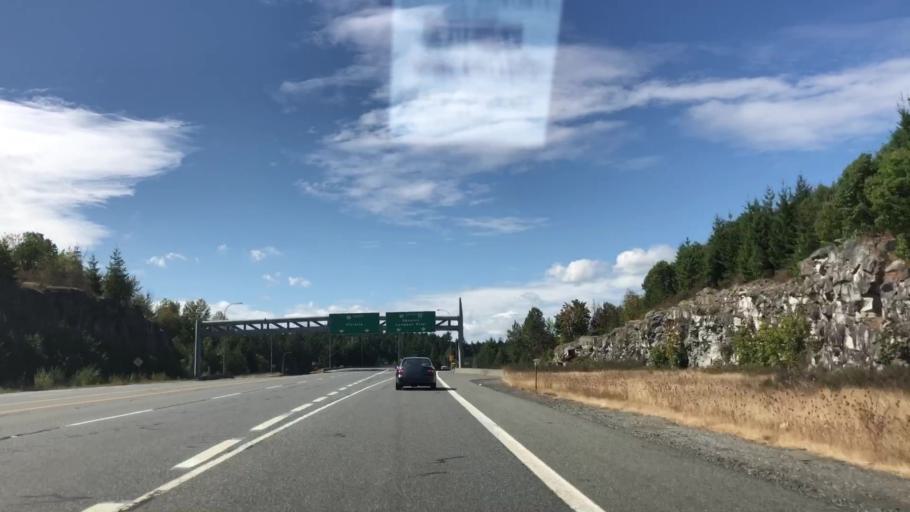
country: CA
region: British Columbia
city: Nanaimo
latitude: 49.1122
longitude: -123.8959
